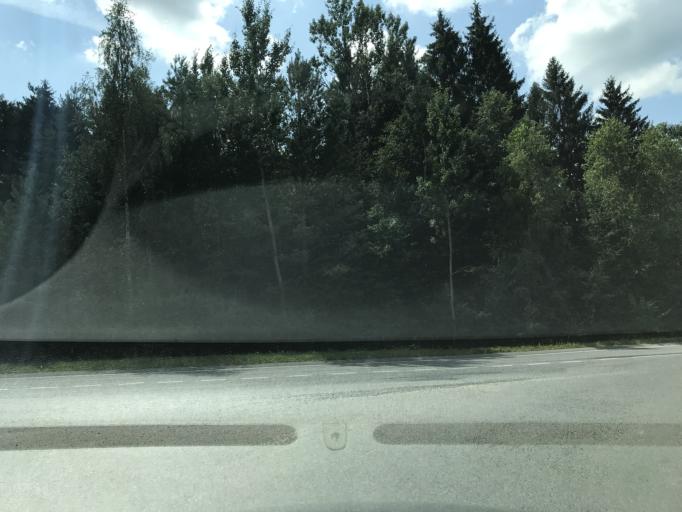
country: BY
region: Minsk
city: Rakaw
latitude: 53.9862
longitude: 26.9898
